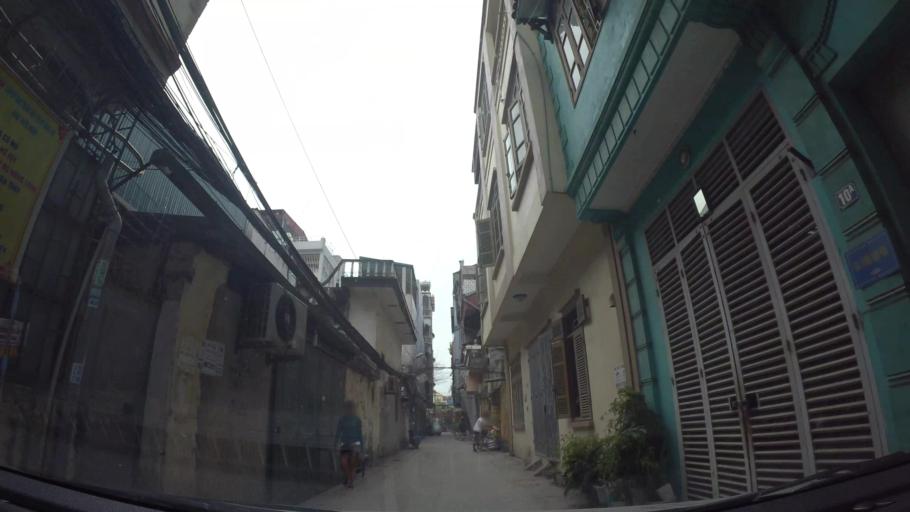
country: VN
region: Ha Noi
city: Ha Dong
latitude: 20.9720
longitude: 105.7660
